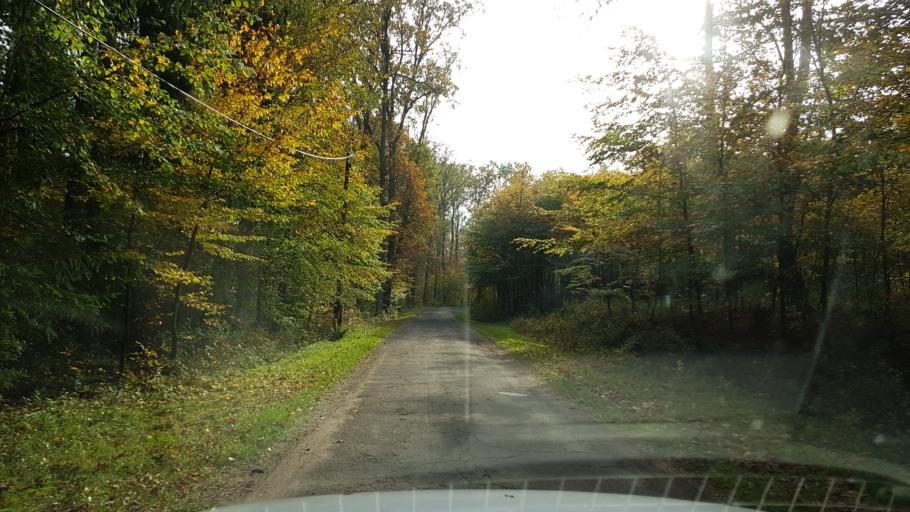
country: PL
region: West Pomeranian Voivodeship
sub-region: Powiat lobeski
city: Wegorzyno
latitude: 53.5086
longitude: 15.4958
